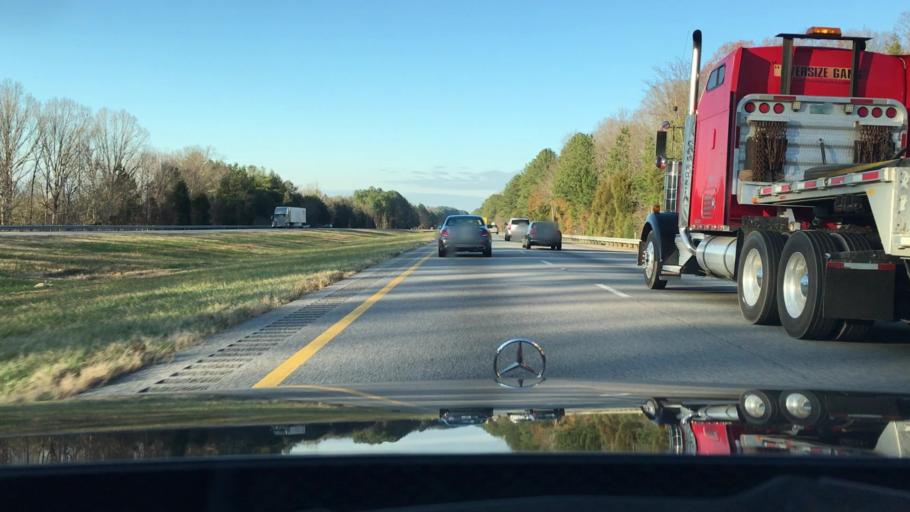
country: US
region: South Carolina
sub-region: Chester County
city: Eureka Mill
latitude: 34.7179
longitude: -81.0319
